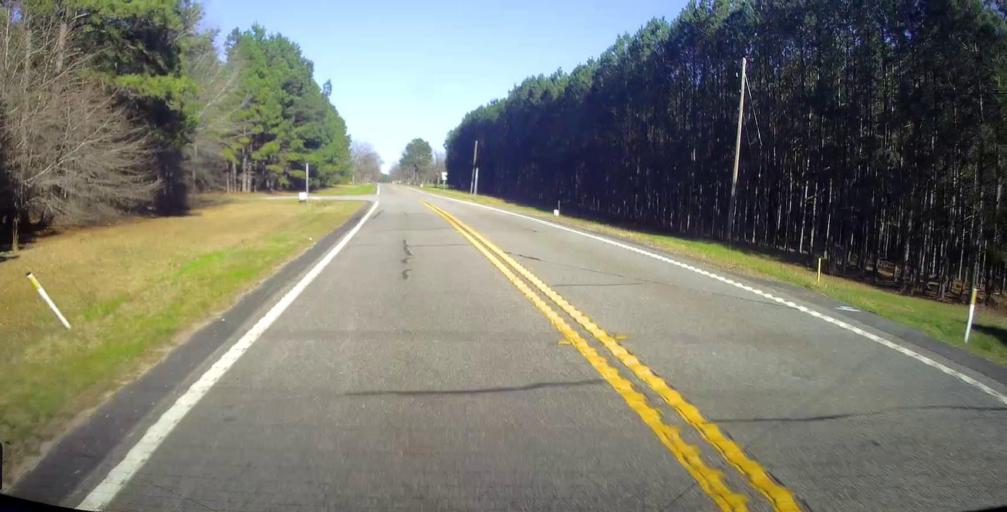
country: US
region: Georgia
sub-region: Schley County
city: Ellaville
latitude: 32.1826
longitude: -84.2492
